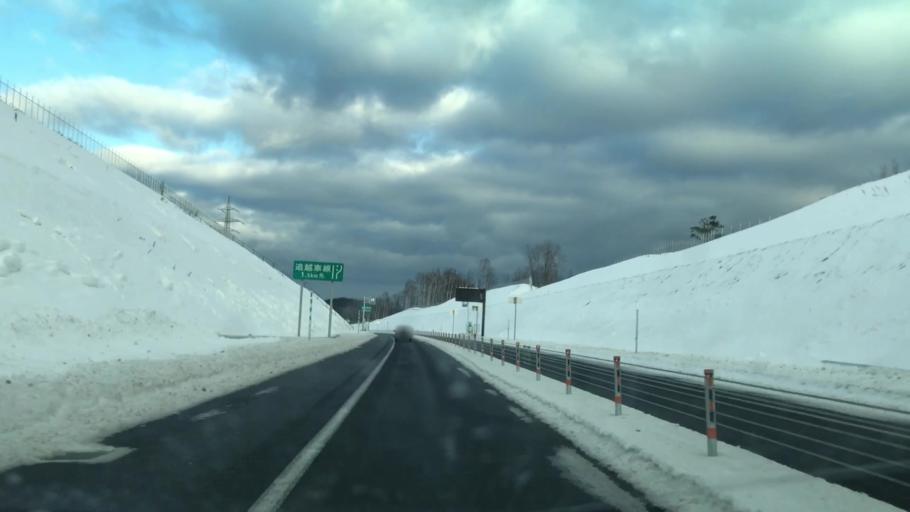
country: JP
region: Hokkaido
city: Otaru
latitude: 43.1890
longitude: 140.9583
